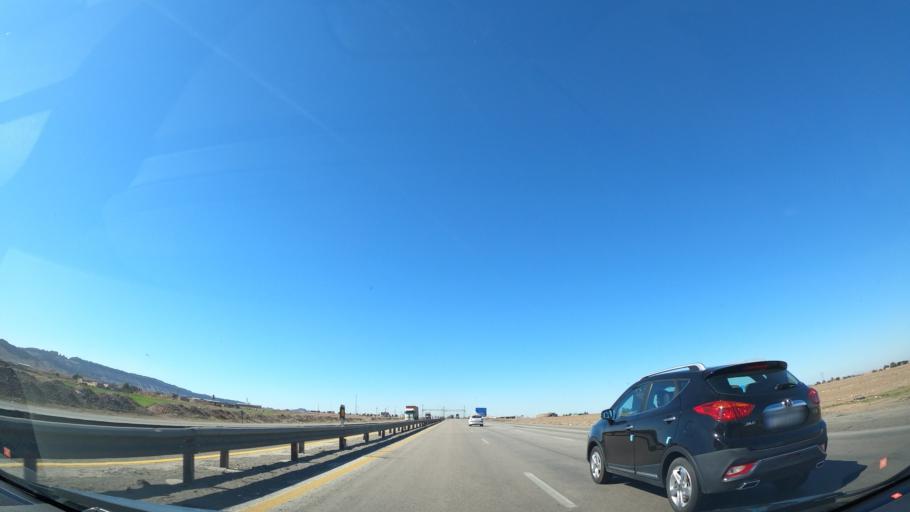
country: IR
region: Qom
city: Qom
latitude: 34.4547
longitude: 51.1020
